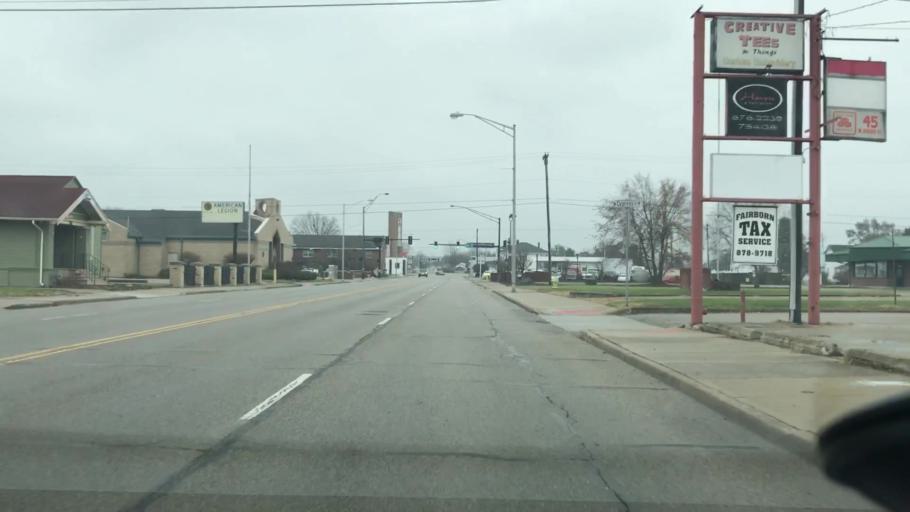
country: US
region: Ohio
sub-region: Greene County
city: Fairborn
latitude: 39.8232
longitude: -84.0277
